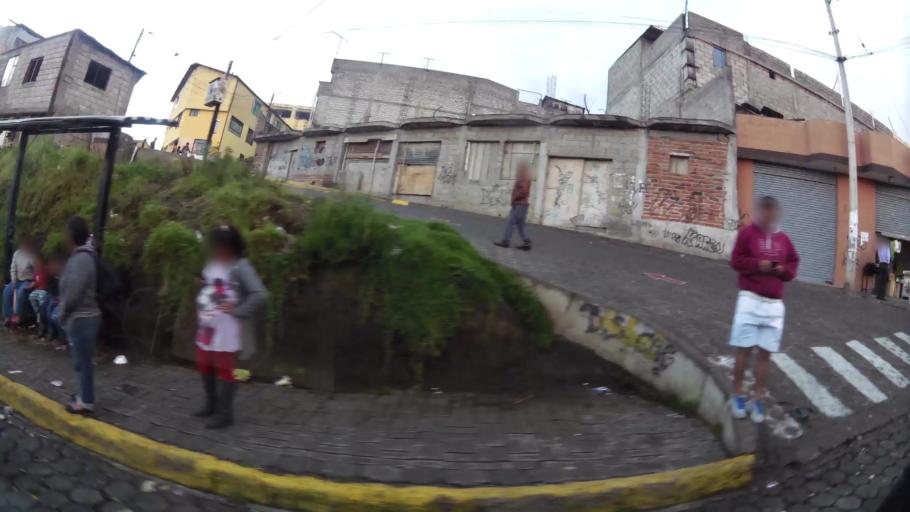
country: EC
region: Pichincha
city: Quito
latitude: -0.0989
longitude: -78.5200
